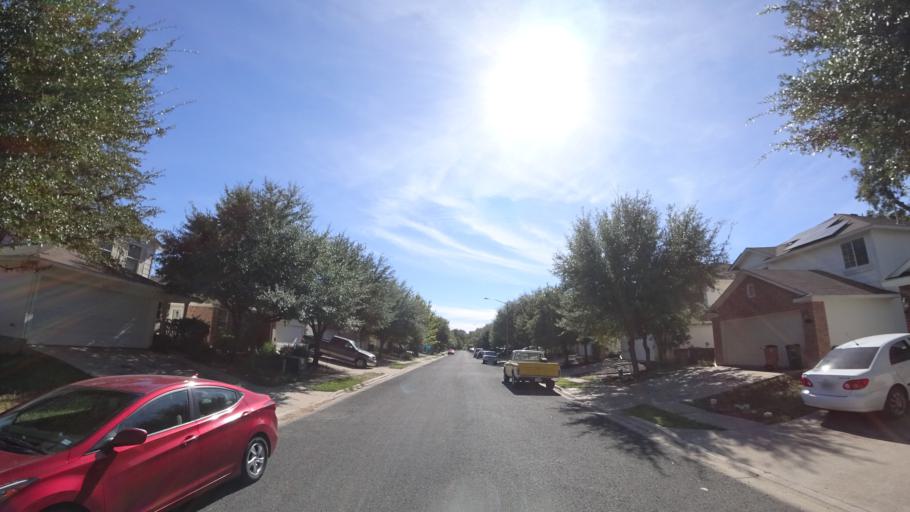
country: US
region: Texas
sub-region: Travis County
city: Austin
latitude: 30.2598
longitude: -97.6860
